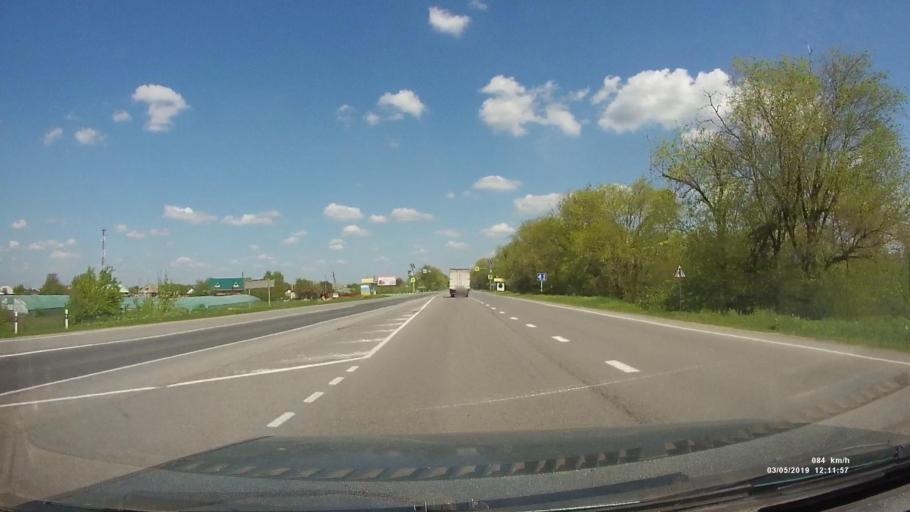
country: RU
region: Rostov
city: Bagayevskaya
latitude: 47.3159
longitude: 40.5425
